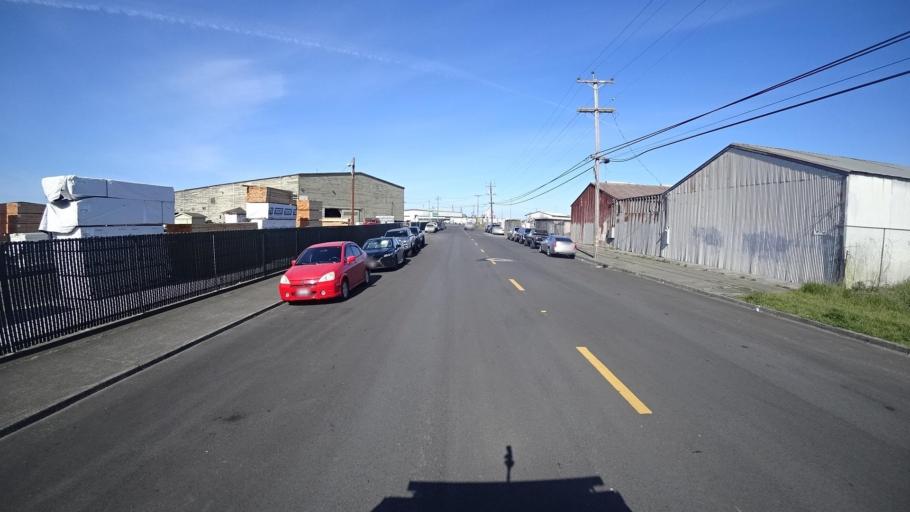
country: US
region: California
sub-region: Humboldt County
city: Eureka
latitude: 40.7983
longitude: -124.1795
